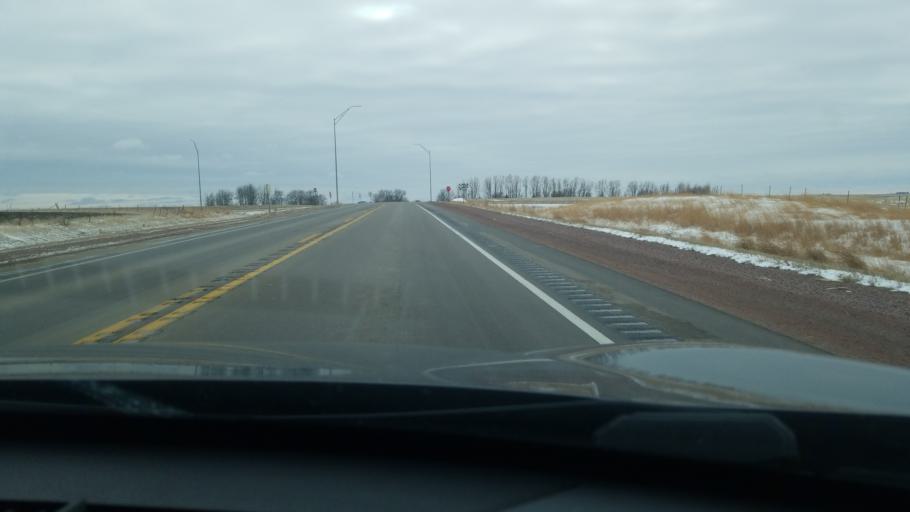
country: US
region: South Dakota
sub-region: Lincoln County
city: Canton
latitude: 43.4345
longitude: -96.4292
